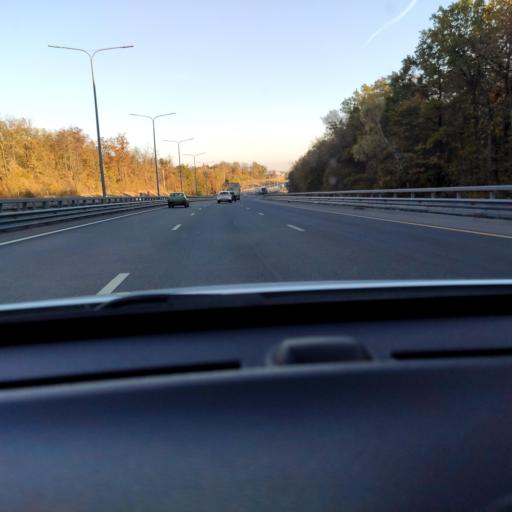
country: RU
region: Voronezj
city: Ramon'
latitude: 51.8310
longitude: 39.2412
